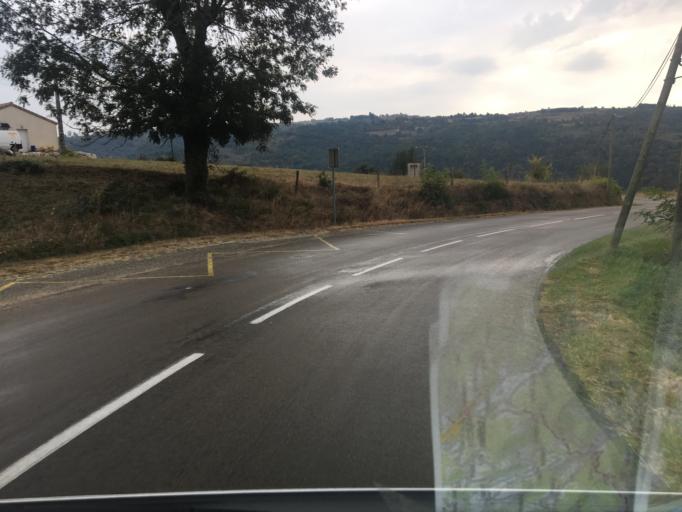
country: FR
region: Rhone-Alpes
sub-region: Departement de l'Ardeche
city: Saint-Felicien
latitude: 45.0548
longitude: 4.7068
